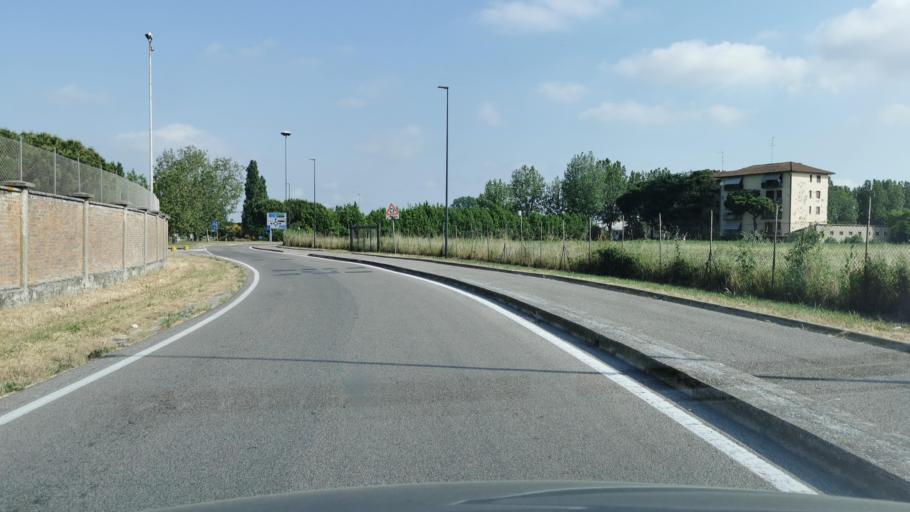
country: IT
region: Emilia-Romagna
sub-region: Provincia di Ravenna
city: Ravenna
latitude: 44.4258
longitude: 12.2164
